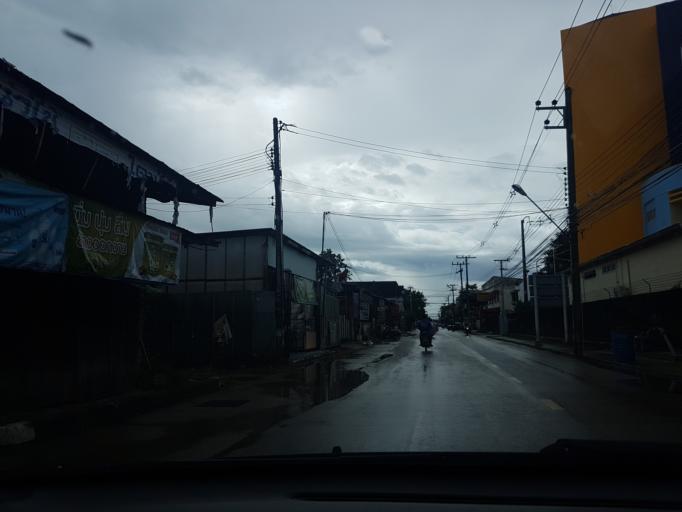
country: TH
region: Lampang
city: Lampang
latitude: 18.2839
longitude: 99.4742
